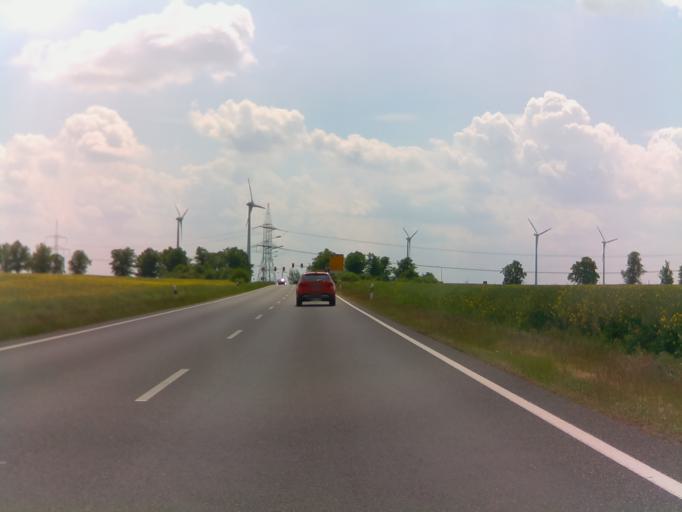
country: DE
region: Brandenburg
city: Nauen
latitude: 52.6034
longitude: 12.8487
